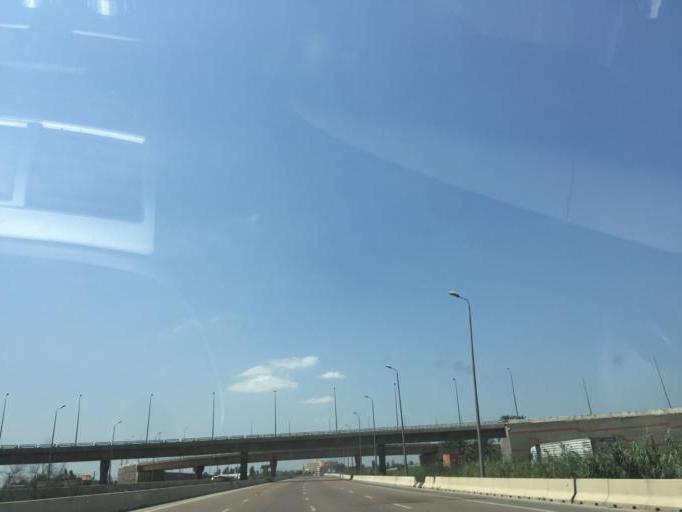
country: EG
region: Al Buhayrah
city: Abu al Matamir
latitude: 30.8877
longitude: 29.8805
